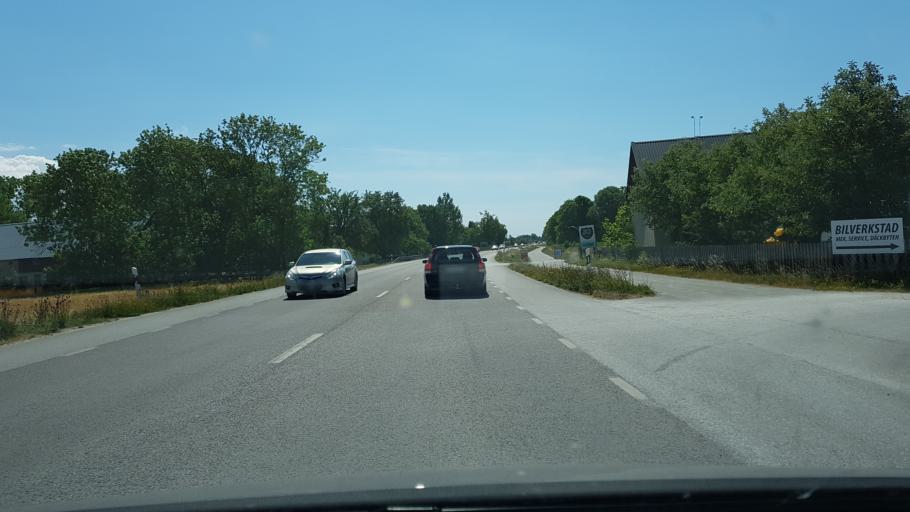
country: SE
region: Gotland
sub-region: Gotland
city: Vibble
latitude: 57.5286
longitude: 18.1759
